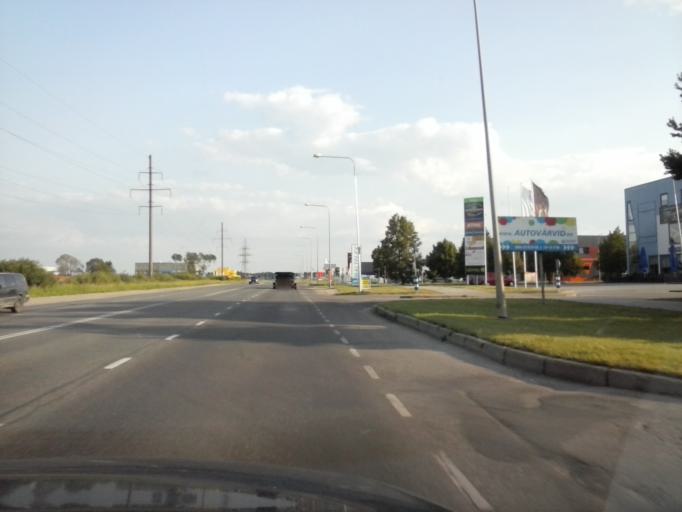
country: EE
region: Tartu
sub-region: Tartu linn
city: Tartu
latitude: 58.3493
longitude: 26.7409
